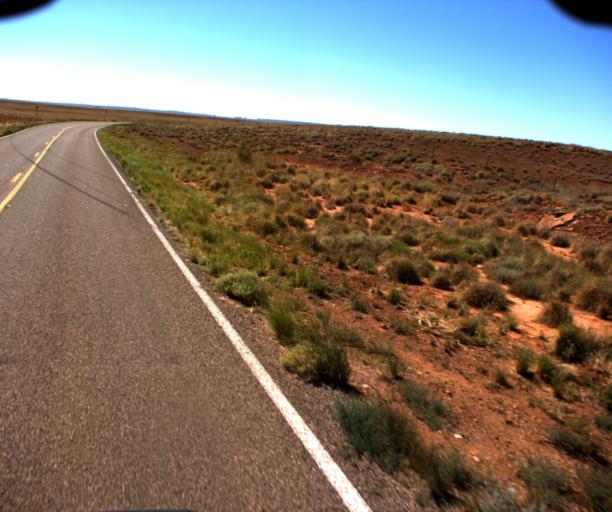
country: US
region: Arizona
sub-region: Coconino County
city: LeChee
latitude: 35.1736
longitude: -110.9206
